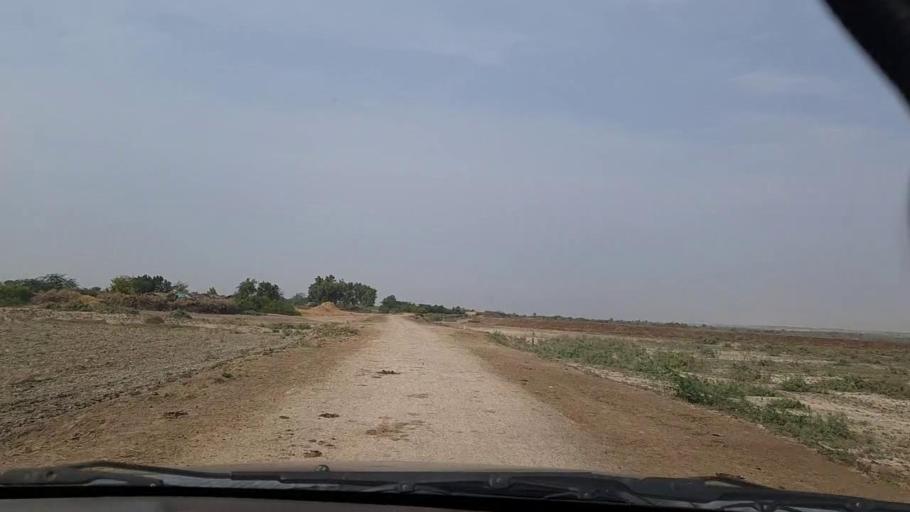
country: PK
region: Sindh
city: Thatta
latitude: 24.5751
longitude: 67.8525
